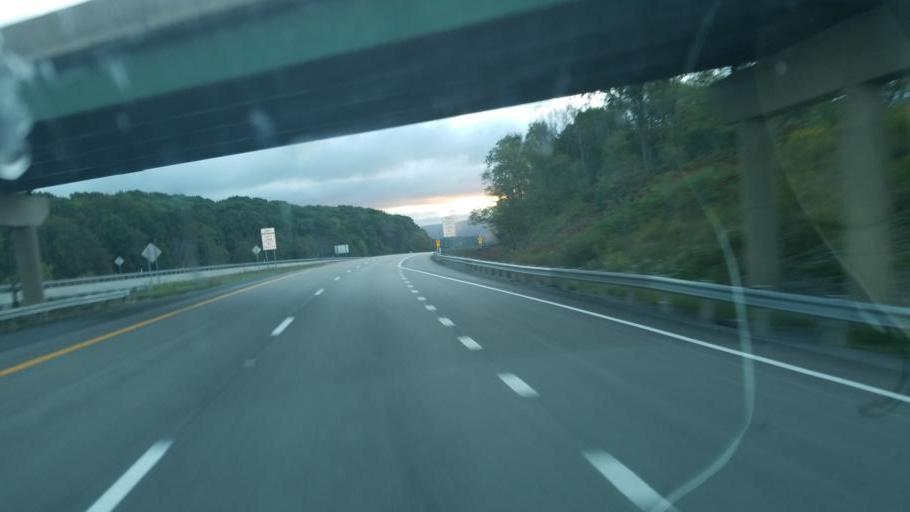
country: US
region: West Virginia
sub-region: Preston County
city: Terra Alta
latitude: 39.6627
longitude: -79.4895
